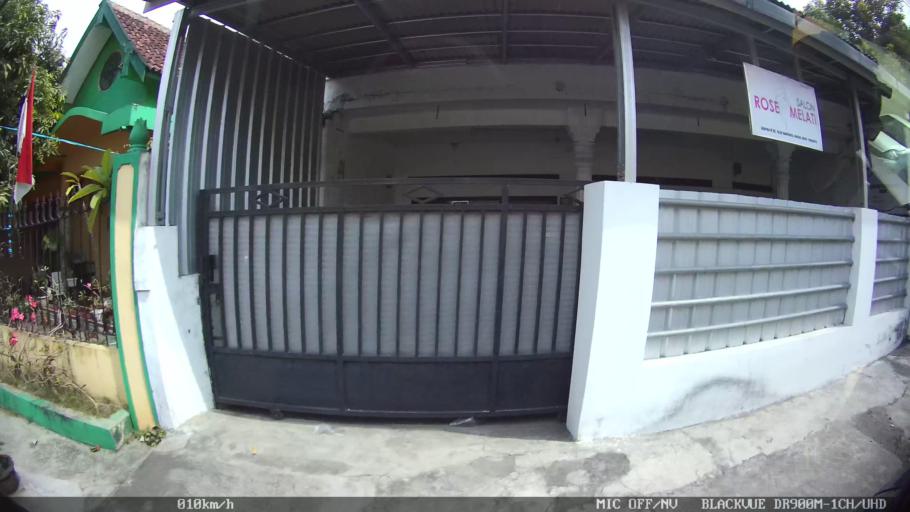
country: ID
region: Daerah Istimewa Yogyakarta
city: Gamping Lor
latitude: -7.8056
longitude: 110.3337
